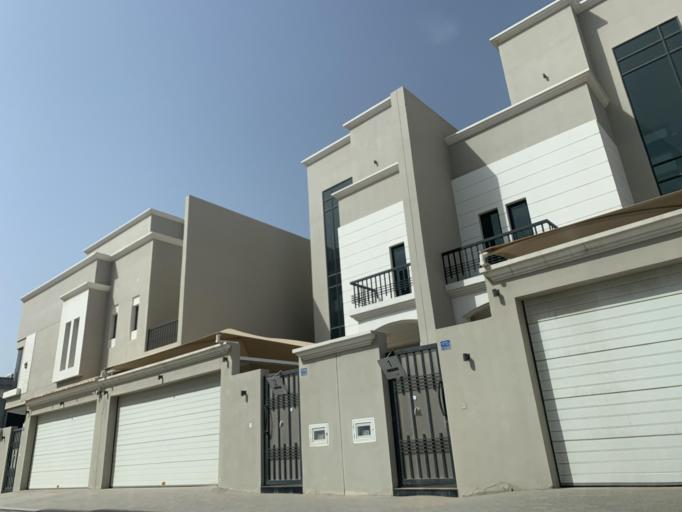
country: BH
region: Manama
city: Jidd Hafs
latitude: 26.2099
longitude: 50.5128
